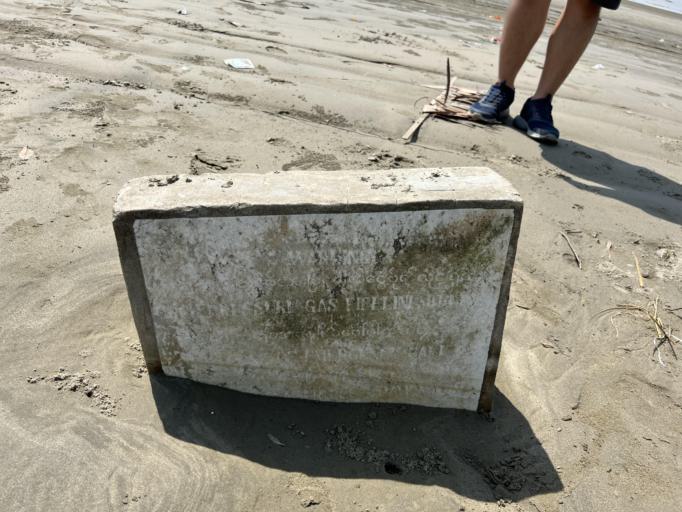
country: MM
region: Ayeyarwady
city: Pyapon
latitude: 15.8985
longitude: 95.6150
